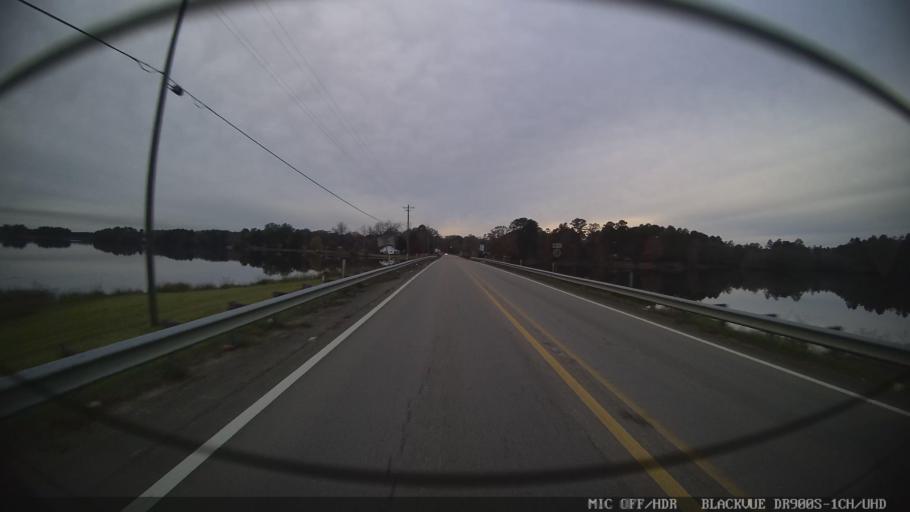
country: US
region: Mississippi
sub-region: Clarke County
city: Quitman
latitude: 32.0396
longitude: -88.7097
